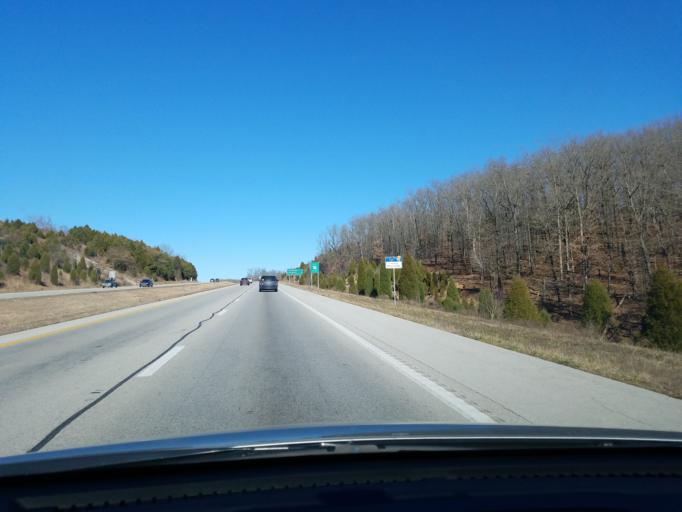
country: US
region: Missouri
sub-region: Taney County
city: Merriam Woods
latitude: 36.7878
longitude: -93.2246
